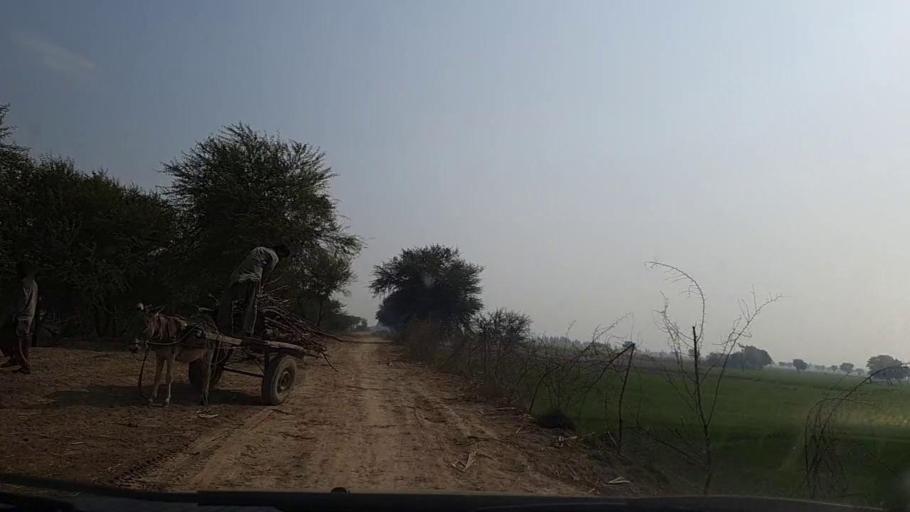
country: PK
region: Sindh
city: Sanghar
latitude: 26.0445
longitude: 68.9906
